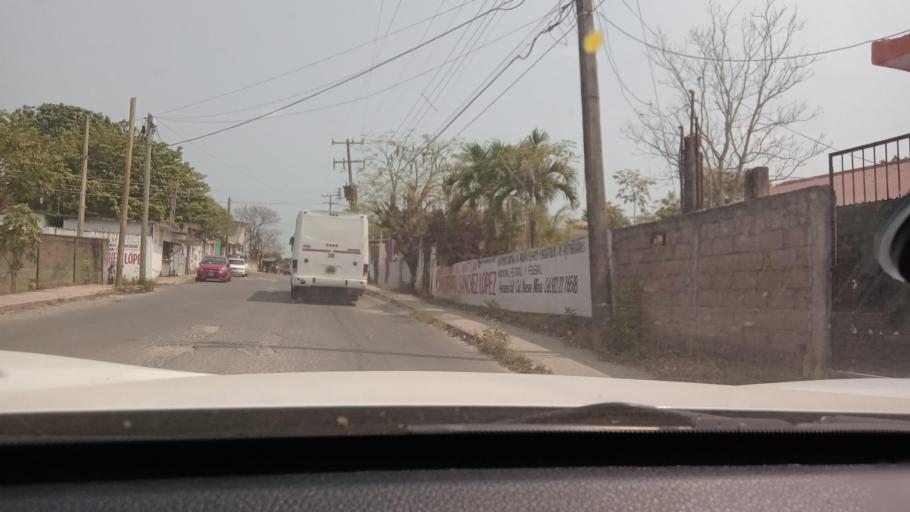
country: MX
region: Veracruz
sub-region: Minatitlan
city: Las Lomas
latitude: 17.9756
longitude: -94.5694
